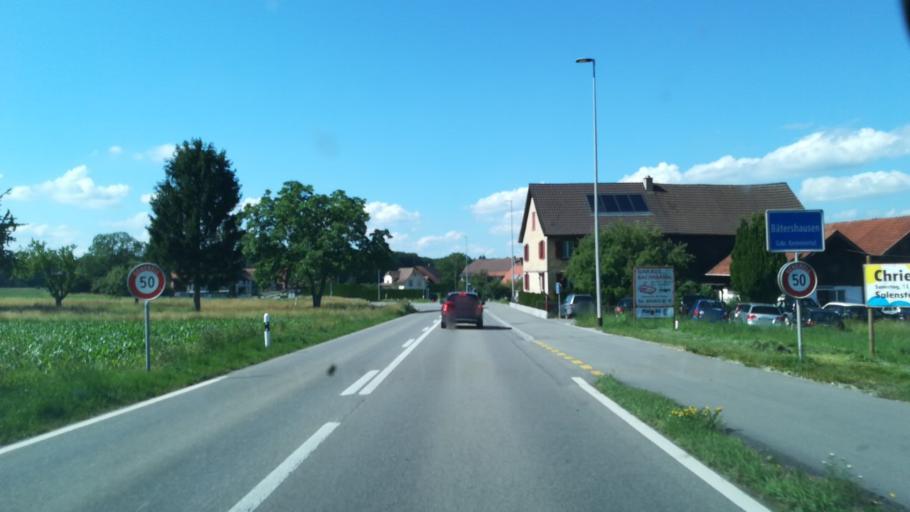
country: CH
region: Thurgau
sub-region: Kreuzlingen District
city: Kreuzlingen
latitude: 47.6288
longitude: 9.1671
